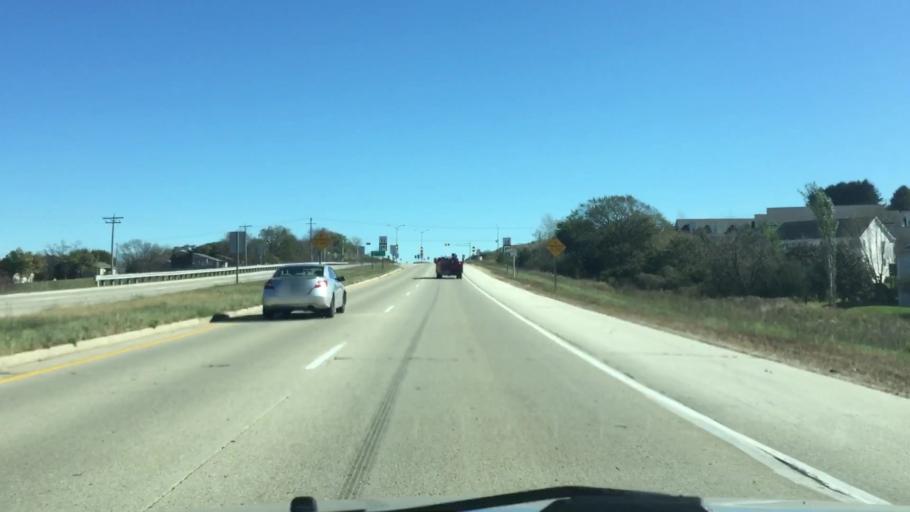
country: US
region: Wisconsin
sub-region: Waukesha County
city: Waukesha
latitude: 42.9768
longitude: -88.2606
